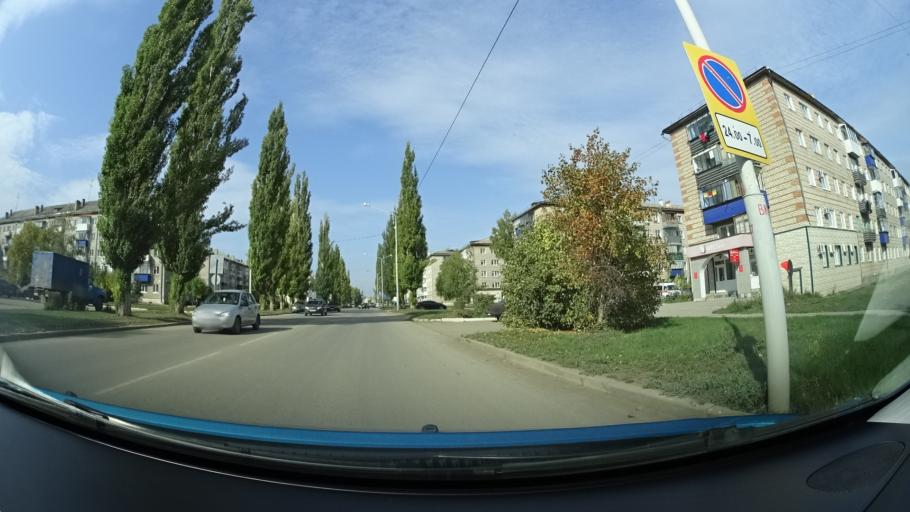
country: RU
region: Bashkortostan
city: Tuymazy
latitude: 54.6009
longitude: 53.7033
